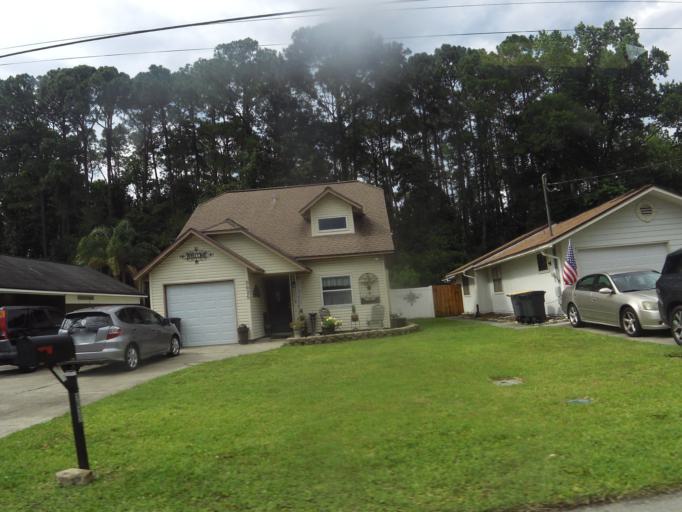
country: US
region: Florida
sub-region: Duval County
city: Jacksonville
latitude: 30.2900
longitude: -81.6069
